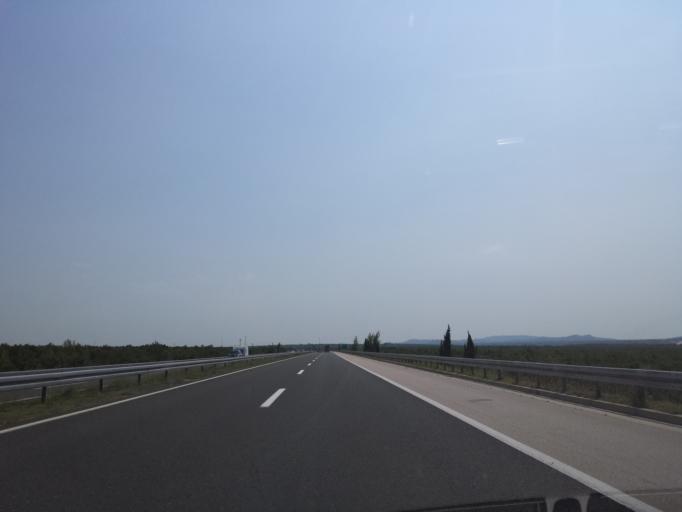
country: HR
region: Zadarska
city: Benkovac
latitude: 44.0291
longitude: 15.5662
